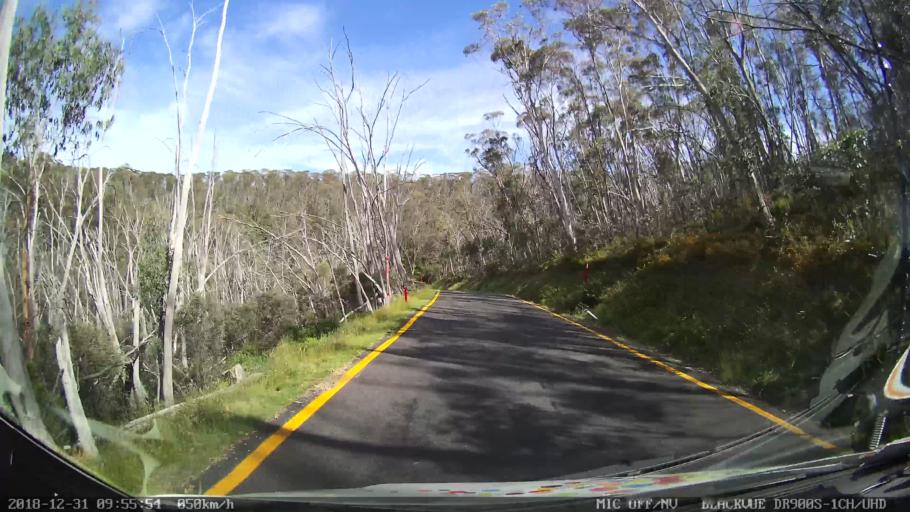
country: AU
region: New South Wales
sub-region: Snowy River
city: Jindabyne
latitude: -36.5311
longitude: 148.2272
